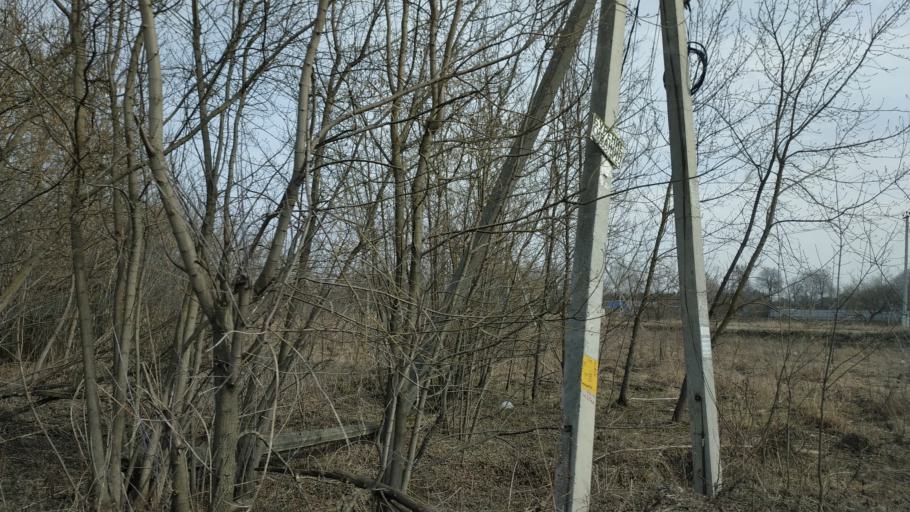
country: RU
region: Moskovskaya
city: Beloozerskiy
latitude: 55.3985
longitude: 38.3833
